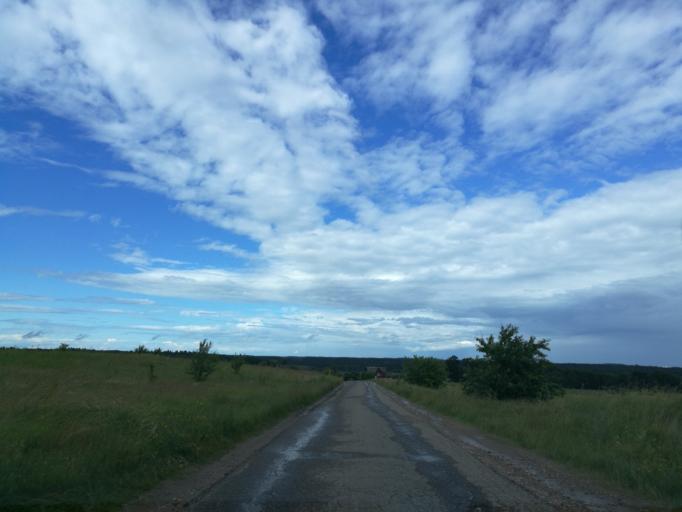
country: LT
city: Lentvaris
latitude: 54.6849
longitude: 25.0247
